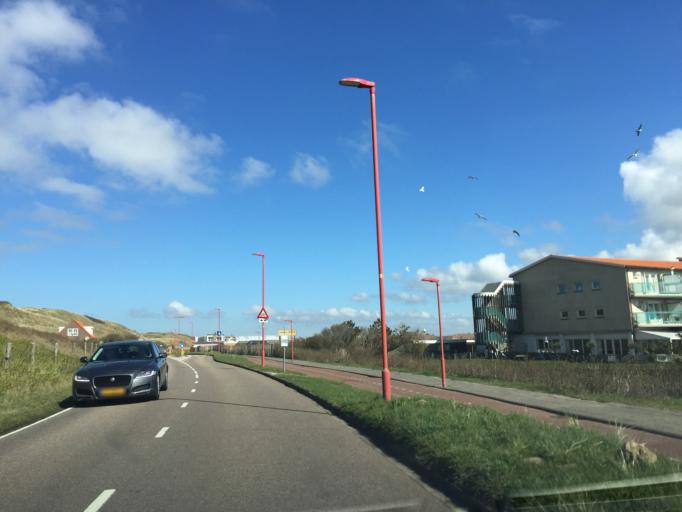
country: NL
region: North Holland
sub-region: Gemeente Den Helder
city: Den Helder
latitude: 52.8969
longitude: 4.7181
